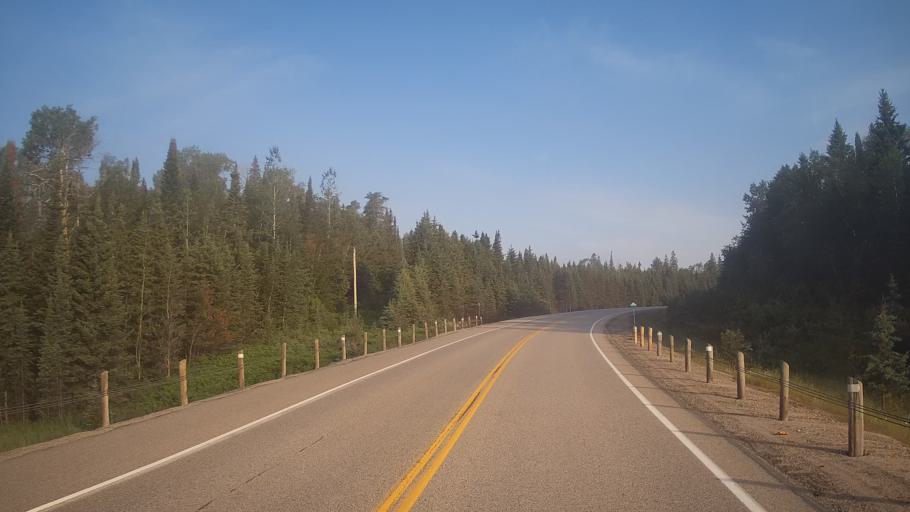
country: CA
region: Ontario
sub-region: Rainy River District
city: Atikokan
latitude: 49.3194
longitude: -91.3962
